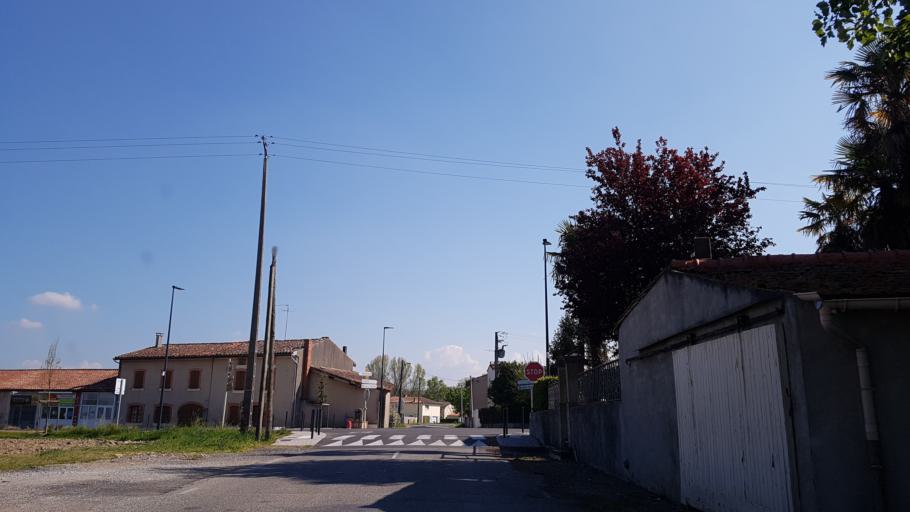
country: FR
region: Midi-Pyrenees
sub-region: Departement de l'Ariege
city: La Tour-du-Crieu
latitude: 43.0938
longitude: 1.7202
